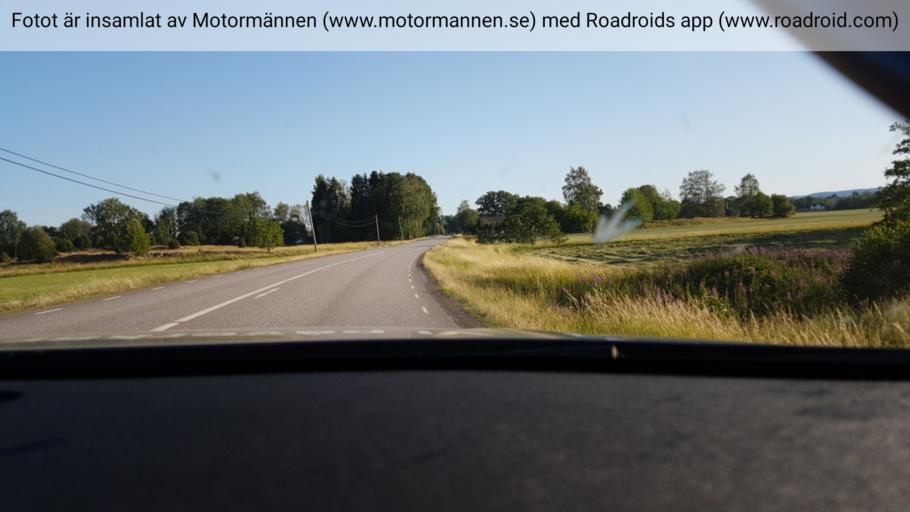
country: SE
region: Vaestra Goetaland
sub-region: Skovde Kommun
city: Stopen
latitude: 58.5153
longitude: 13.9764
